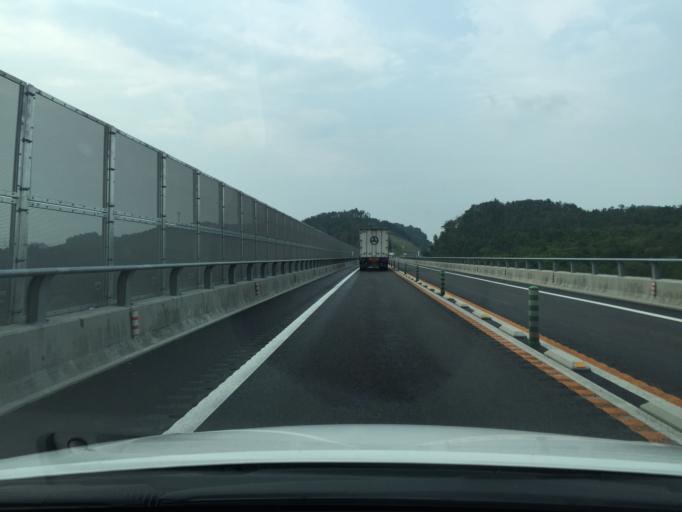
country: JP
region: Fukushima
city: Namie
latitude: 37.4321
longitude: 140.9595
